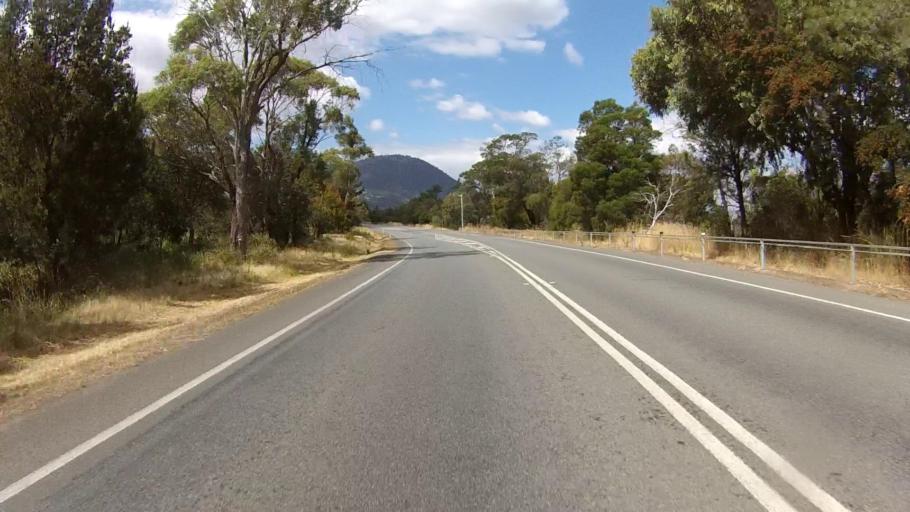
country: AU
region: Tasmania
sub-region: Brighton
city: Old Beach
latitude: -42.7765
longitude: 147.2705
